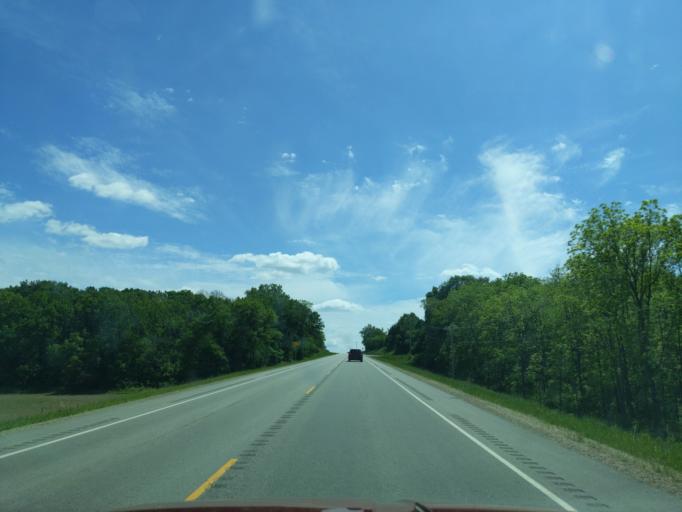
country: US
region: Wisconsin
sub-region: Columbia County
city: Rio
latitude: 43.4461
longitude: -89.3287
